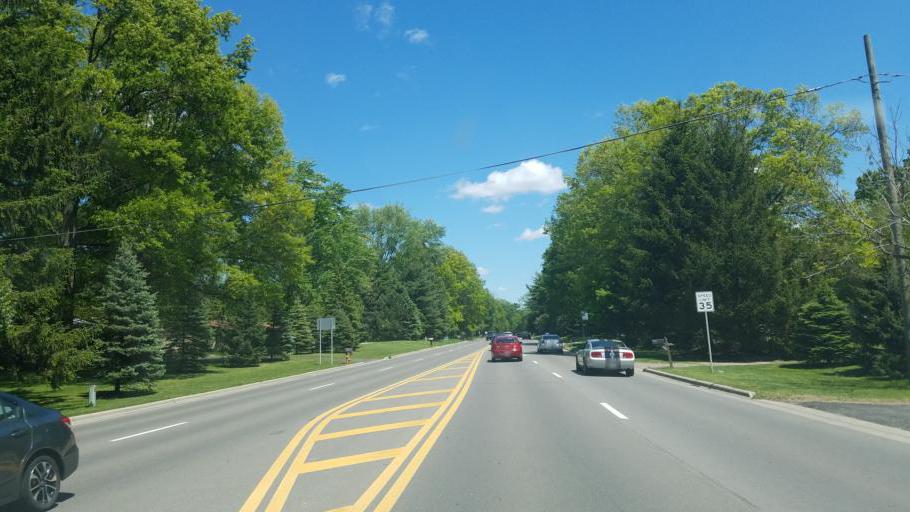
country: US
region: Ohio
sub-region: Franklin County
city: Hilliard
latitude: 40.0276
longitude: -83.1095
